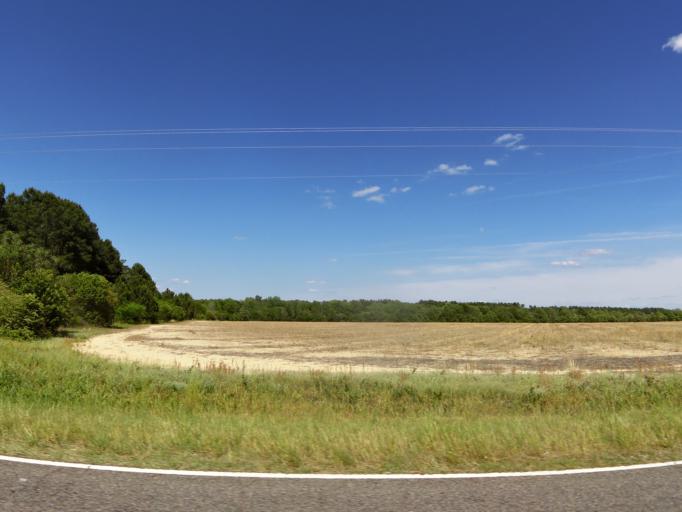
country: US
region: South Carolina
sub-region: Barnwell County
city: Williston
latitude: 33.4432
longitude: -81.4885
